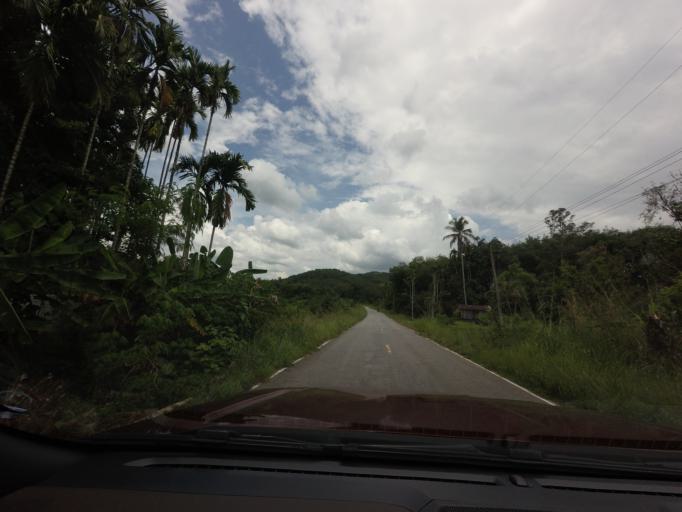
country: TH
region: Narathiwat
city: Chanae
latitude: 6.0428
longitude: 101.6914
